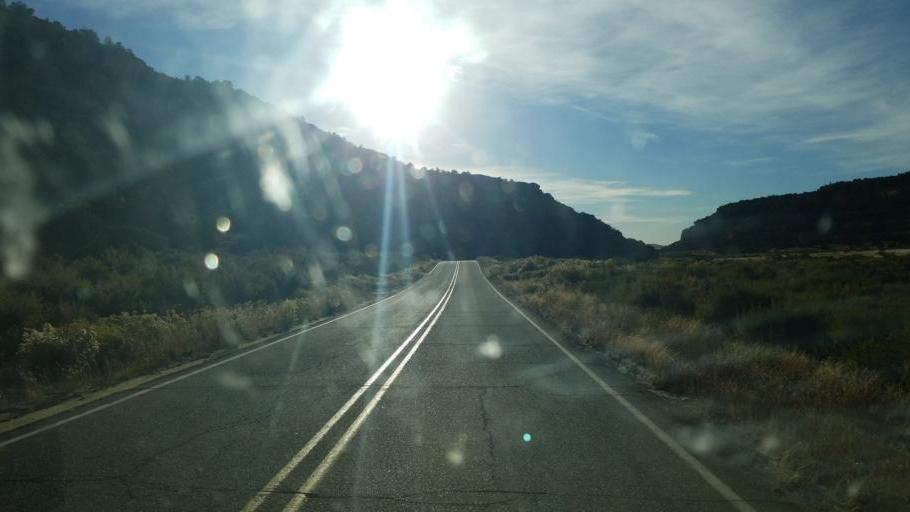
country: US
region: New Mexico
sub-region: San Juan County
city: Bloomfield
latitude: 36.7397
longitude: -107.7262
